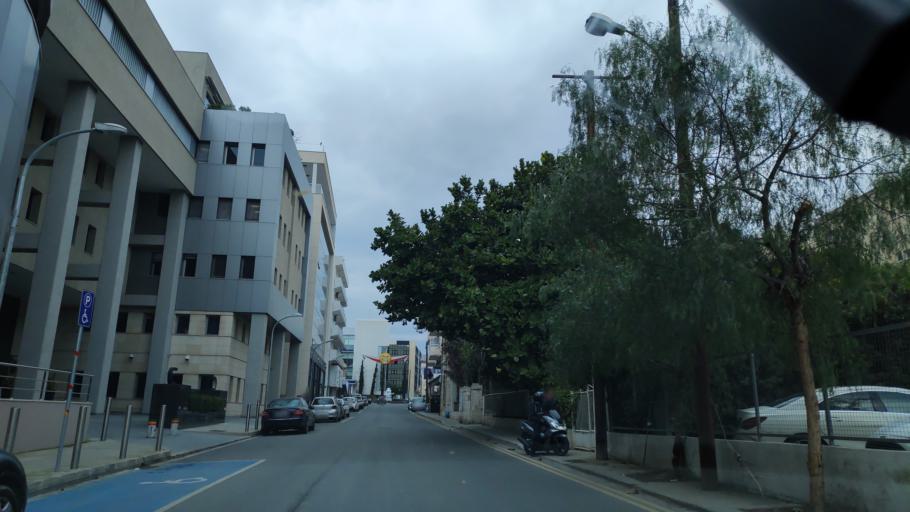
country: CY
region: Limassol
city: Limassol
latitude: 34.6817
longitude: 33.0483
